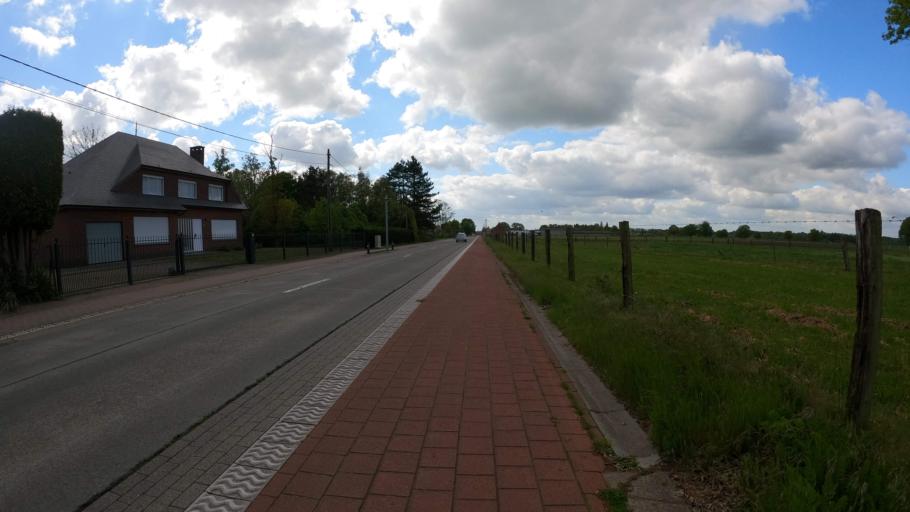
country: BE
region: Flanders
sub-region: Provincie Antwerpen
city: Rijkevorsel
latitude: 51.3122
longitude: 4.7774
